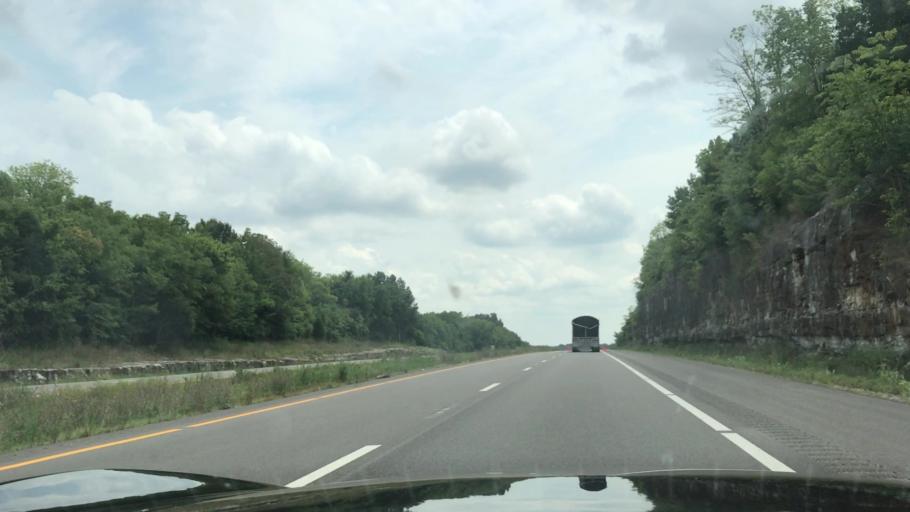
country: US
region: Kentucky
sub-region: Warren County
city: Bowling Green
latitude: 36.9692
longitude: -86.4995
